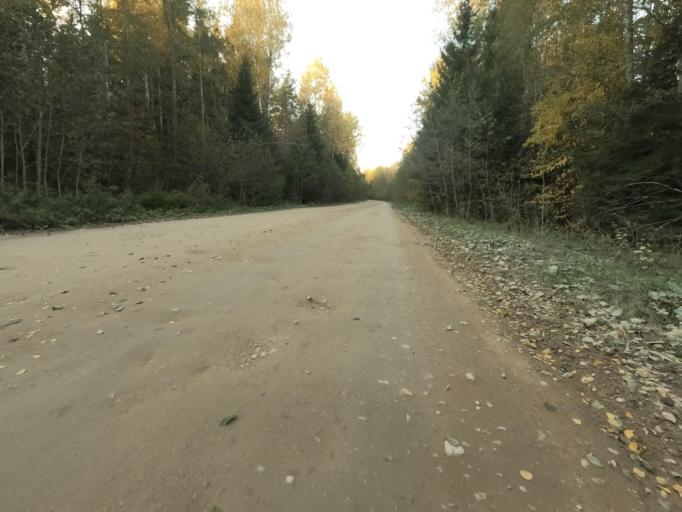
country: RU
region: Leningrad
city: Lyuban'
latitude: 59.0125
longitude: 31.0887
